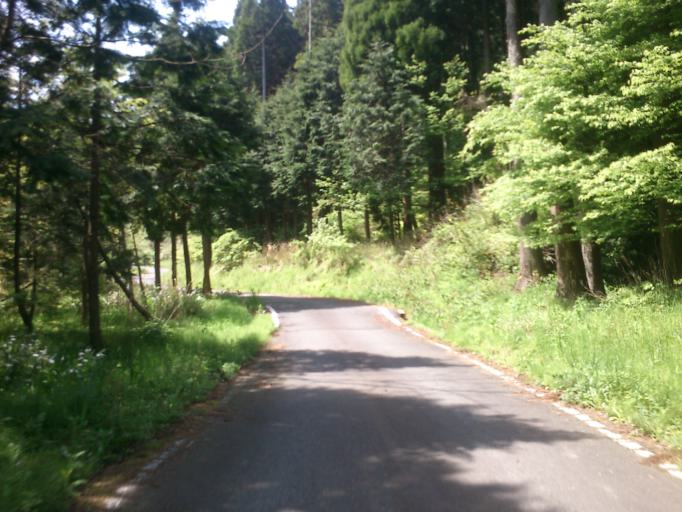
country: JP
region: Kyoto
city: Miyazu
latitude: 35.6660
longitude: 135.2318
